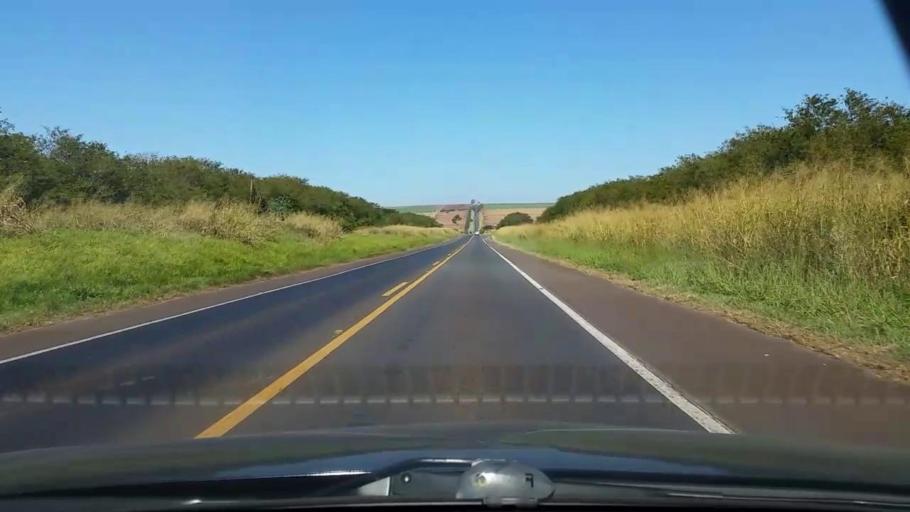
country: BR
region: Sao Paulo
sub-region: Jau
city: Jau
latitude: -22.3651
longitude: -48.5712
